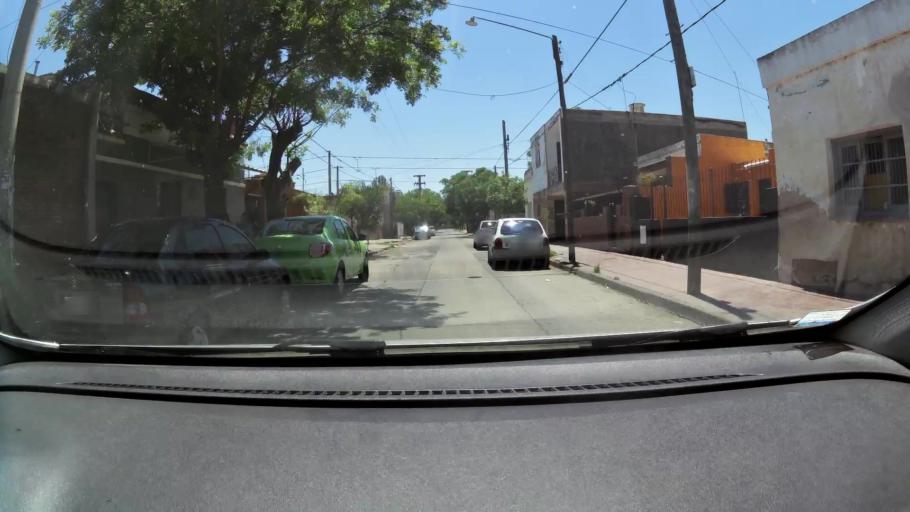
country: AR
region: Cordoba
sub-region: Departamento de Capital
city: Cordoba
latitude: -31.3964
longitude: -64.2064
